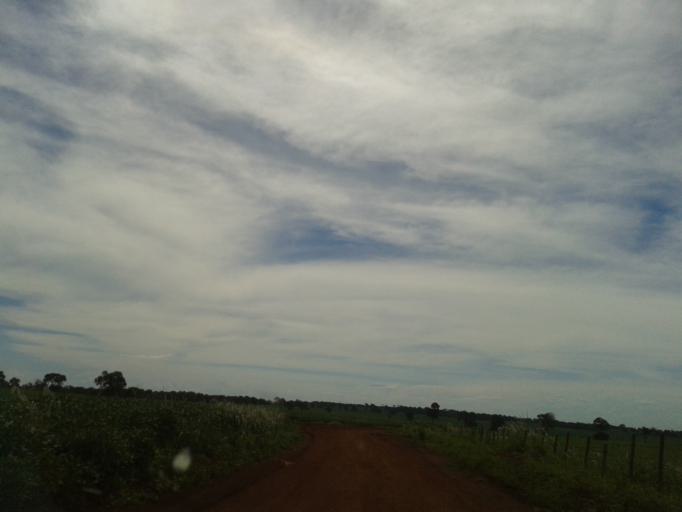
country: BR
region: Minas Gerais
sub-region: Capinopolis
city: Capinopolis
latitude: -18.7460
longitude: -49.8444
